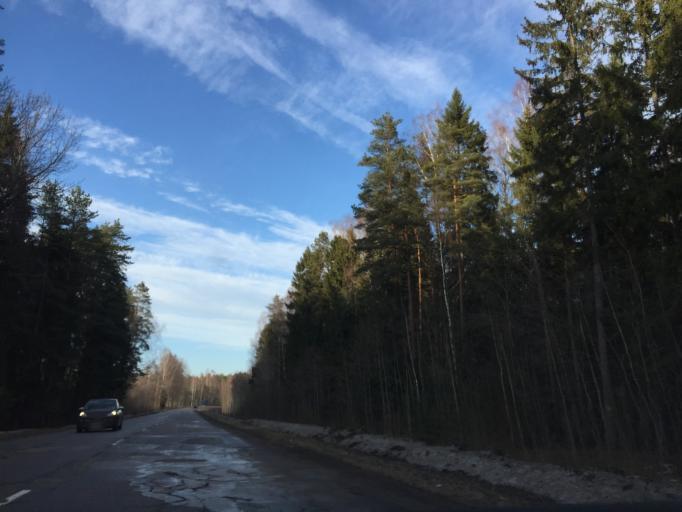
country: LV
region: Kekava
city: Balozi
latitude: 56.7477
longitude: 24.1075
